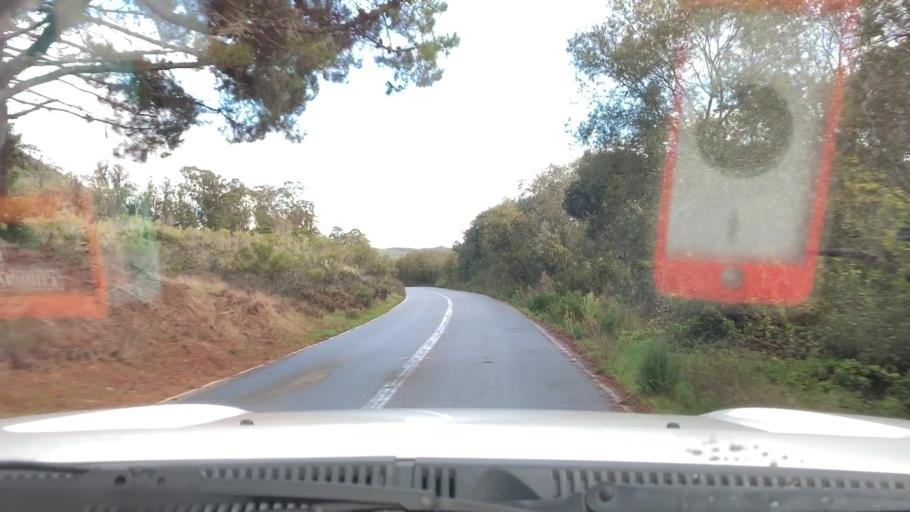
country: US
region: California
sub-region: San Luis Obispo County
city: Morro Bay
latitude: 35.3517
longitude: -120.8311
